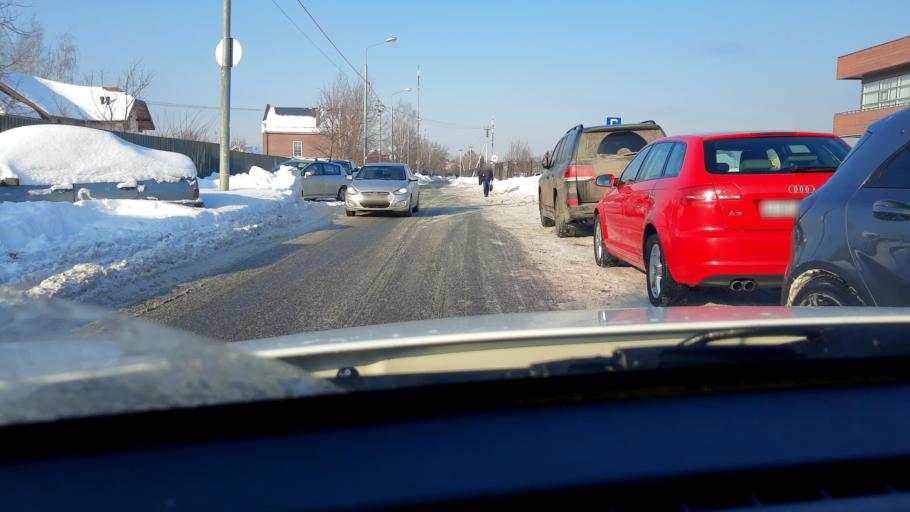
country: RU
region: Moskovskaya
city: Vatutinki
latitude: 55.4955
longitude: 37.3219
